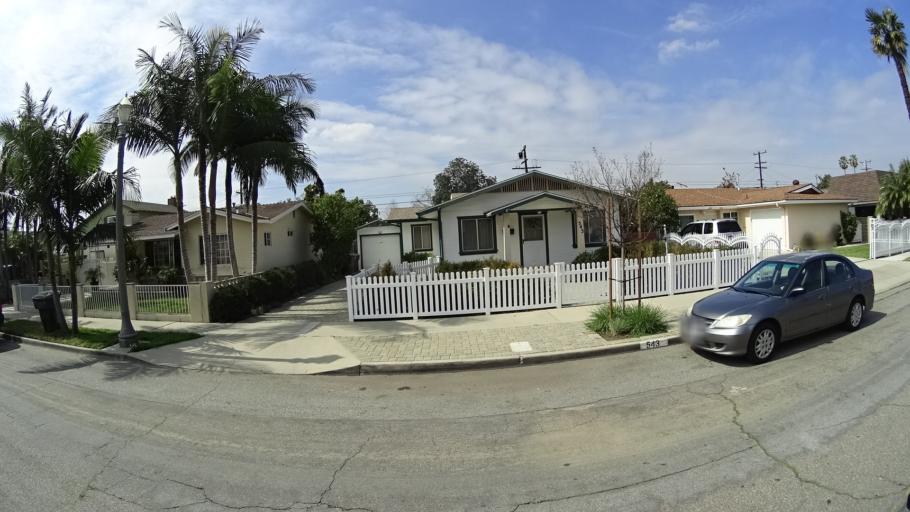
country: US
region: California
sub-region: Orange County
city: Anaheim
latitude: 33.8278
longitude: -117.9196
